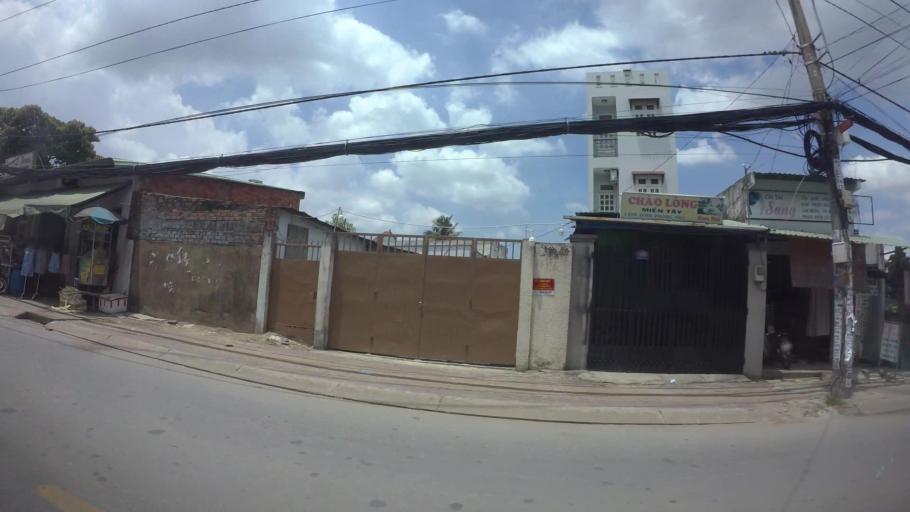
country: VN
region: Ho Chi Minh City
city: Quan Chin
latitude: 10.8362
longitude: 106.7823
